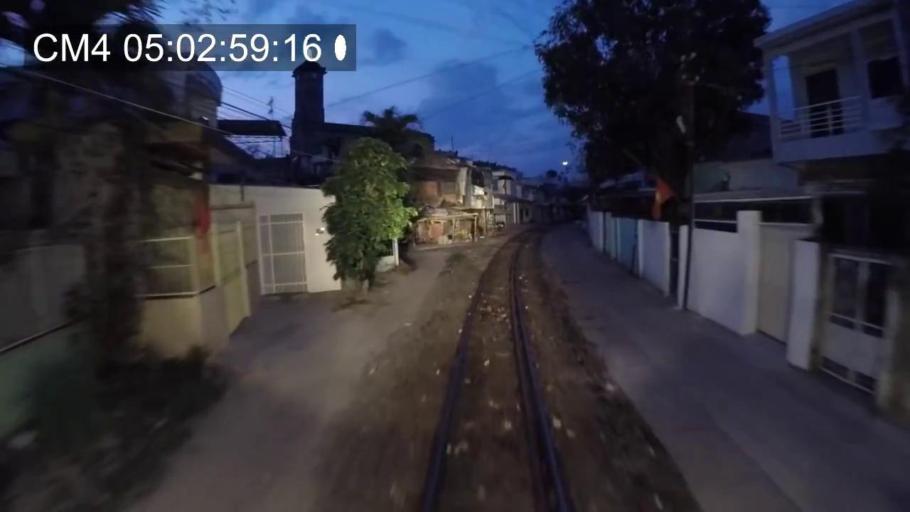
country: VN
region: Khanh Hoa
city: Nha Trang
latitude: 12.2526
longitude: 109.1718
